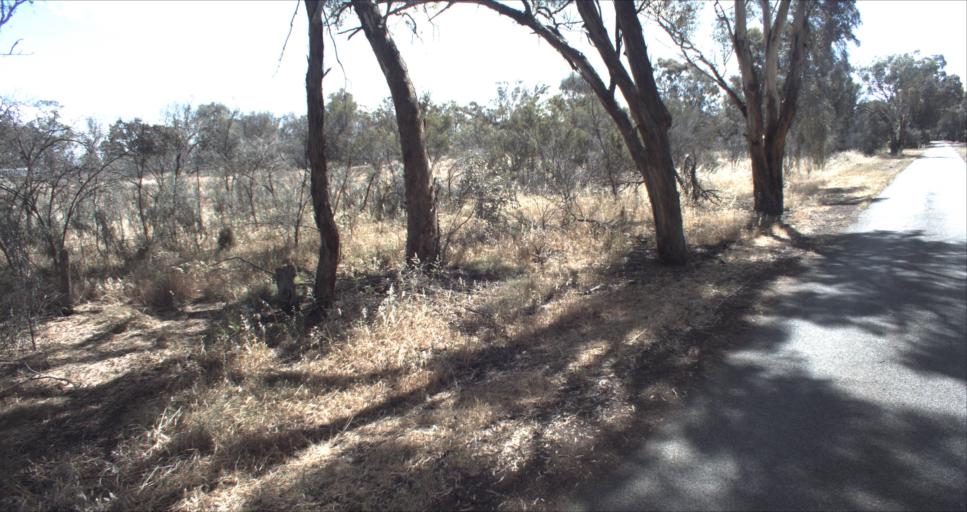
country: AU
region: New South Wales
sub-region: Leeton
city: Leeton
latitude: -34.5162
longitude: 146.2357
